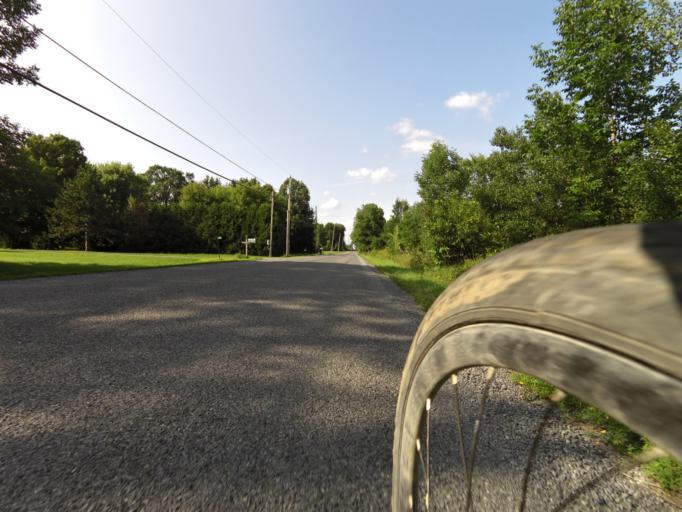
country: CA
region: Ontario
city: Kingston
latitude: 44.3775
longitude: -76.5953
